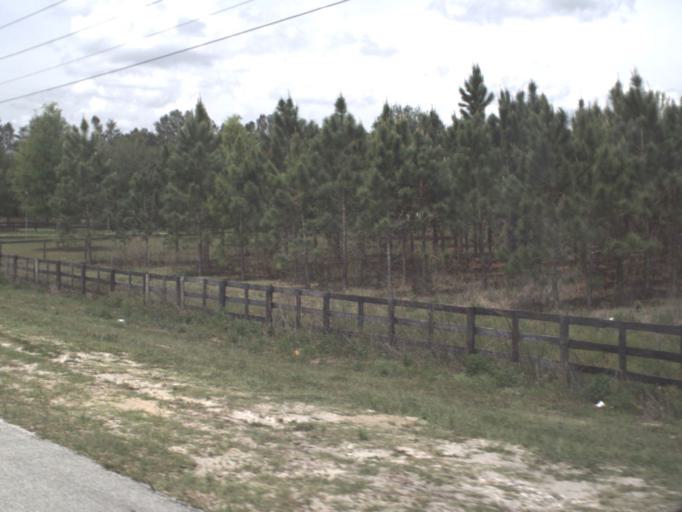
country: US
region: Florida
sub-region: Lake County
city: Mount Plymouth
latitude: 28.8512
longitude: -81.5717
